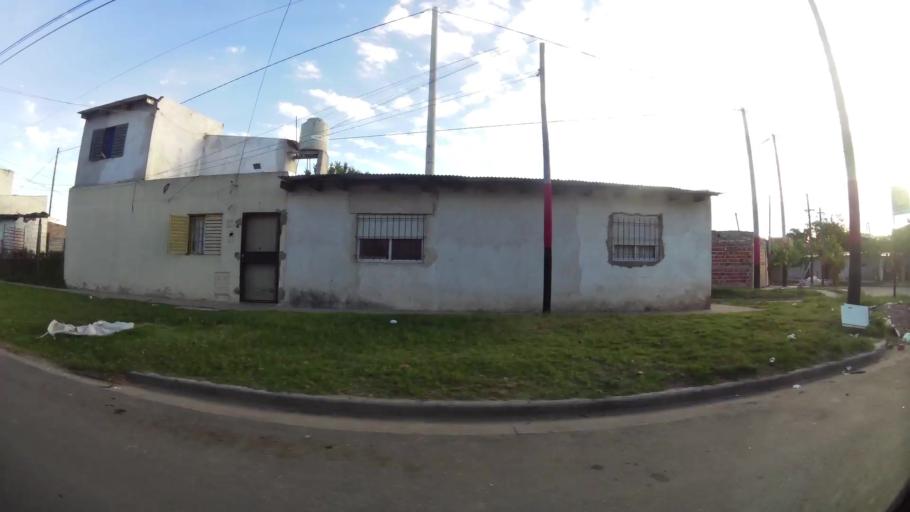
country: AR
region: Santa Fe
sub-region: Departamento de Rosario
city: Rosario
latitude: -32.9799
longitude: -60.6693
